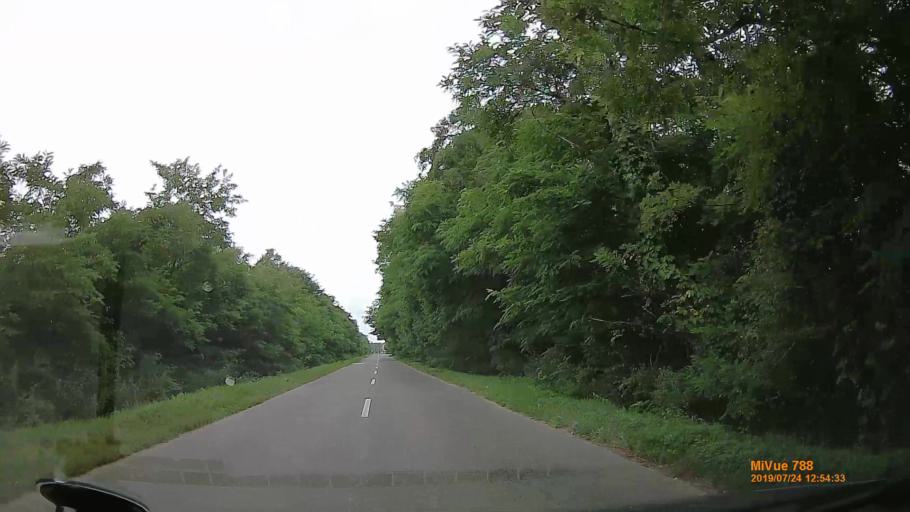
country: HU
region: Szabolcs-Szatmar-Bereg
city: Aranyosapati
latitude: 48.2168
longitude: 22.2980
